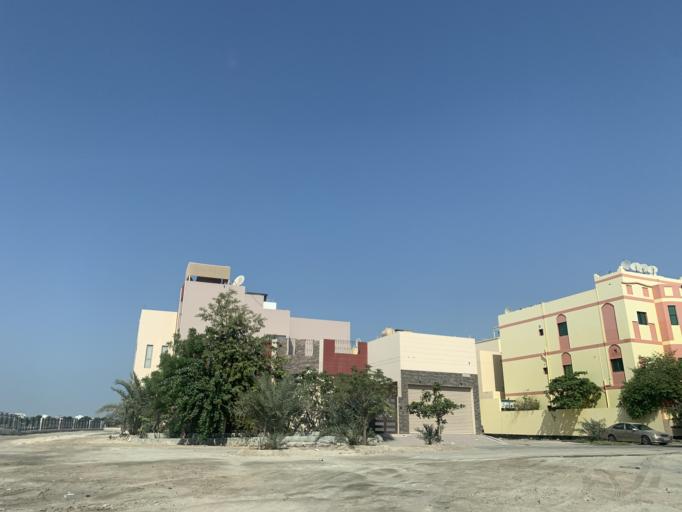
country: BH
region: Central Governorate
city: Madinat Hamad
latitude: 26.1302
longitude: 50.4862
